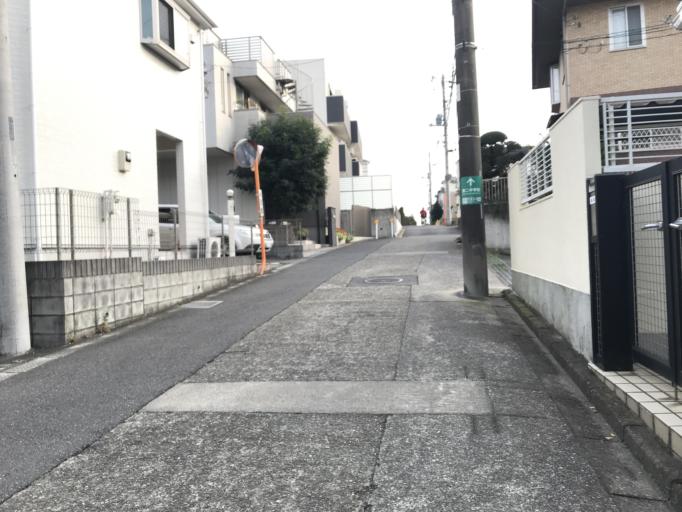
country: JP
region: Chiba
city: Funabashi
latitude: 35.7603
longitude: 140.0016
